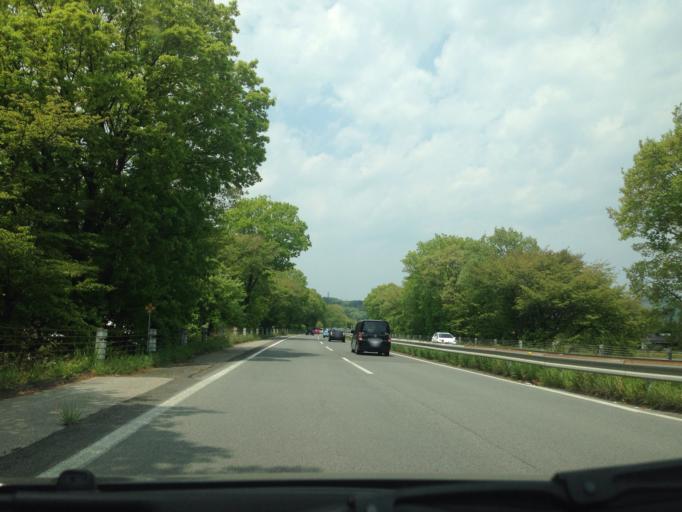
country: JP
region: Tochigi
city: Utsunomiya-shi
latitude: 36.6460
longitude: 139.8392
